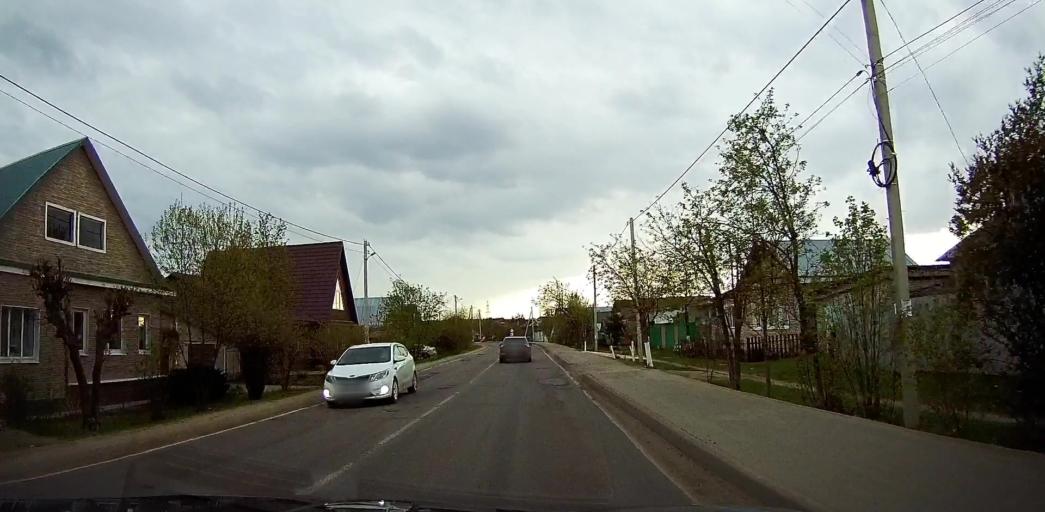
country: RU
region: Moskovskaya
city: Pavlovskiy Posad
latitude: 55.7536
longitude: 38.7023
